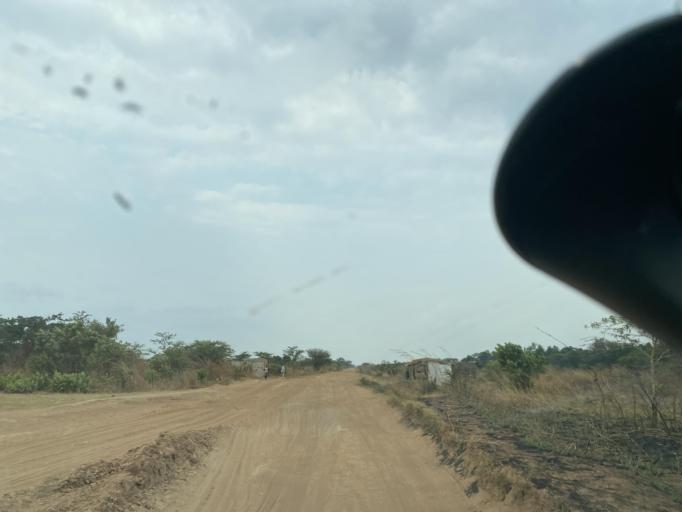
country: ZM
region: Lusaka
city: Lusaka
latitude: -15.2093
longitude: 28.3397
